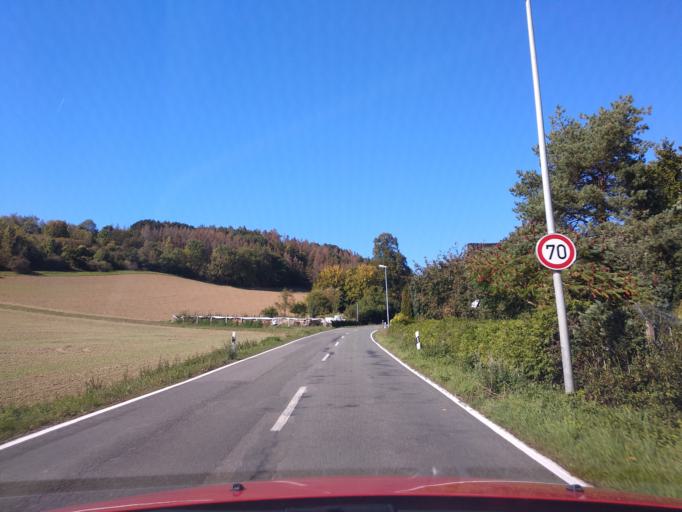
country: DE
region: North Rhine-Westphalia
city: Beverungen
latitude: 51.7149
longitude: 9.2894
